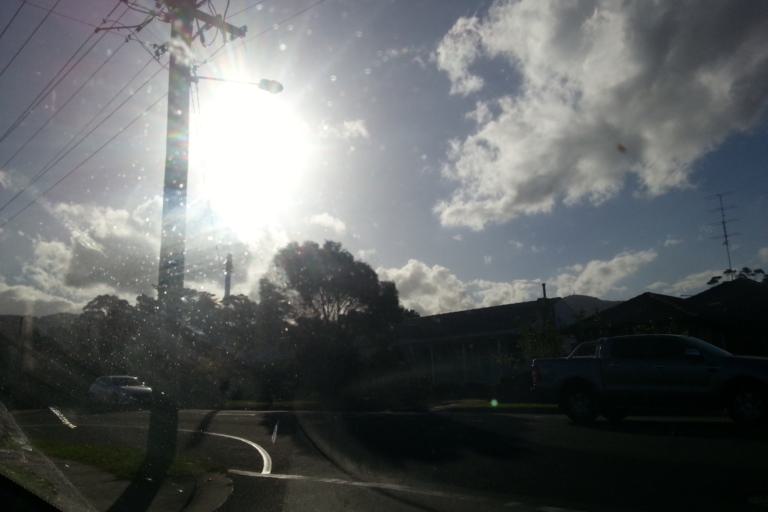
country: AU
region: New South Wales
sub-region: Wollongong
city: Fairy Meadow
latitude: -34.3970
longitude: 150.8872
